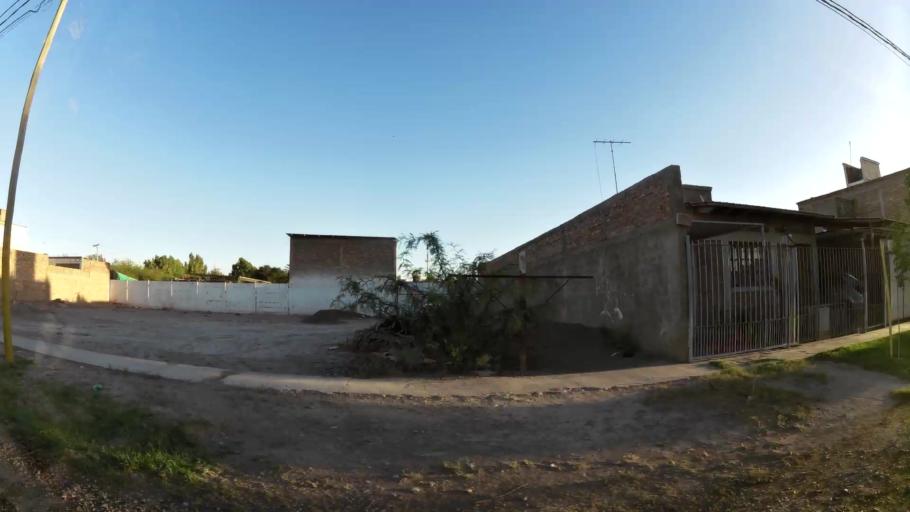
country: AR
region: San Juan
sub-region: Departamento de Santa Lucia
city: Santa Lucia
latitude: -31.5315
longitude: -68.5054
